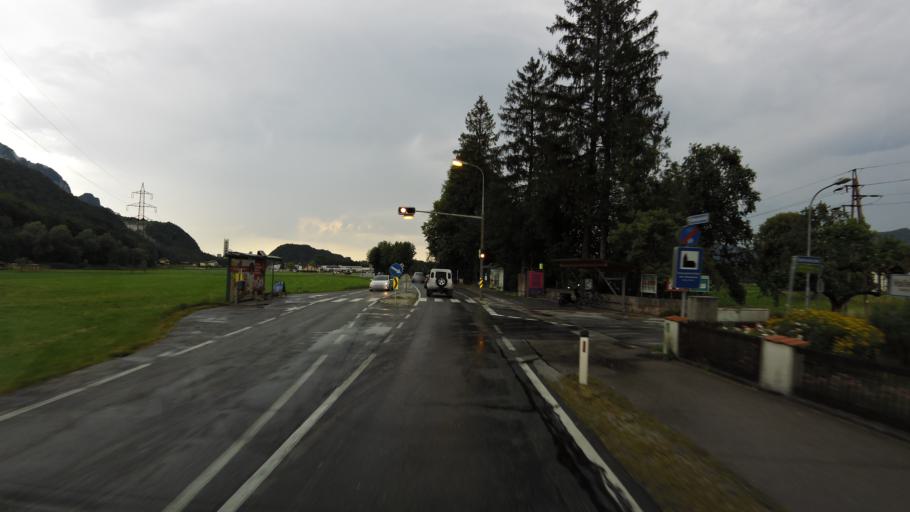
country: AT
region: Salzburg
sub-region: Politischer Bezirk Hallein
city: Puch bei Hallein
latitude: 47.7088
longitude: 13.0678
